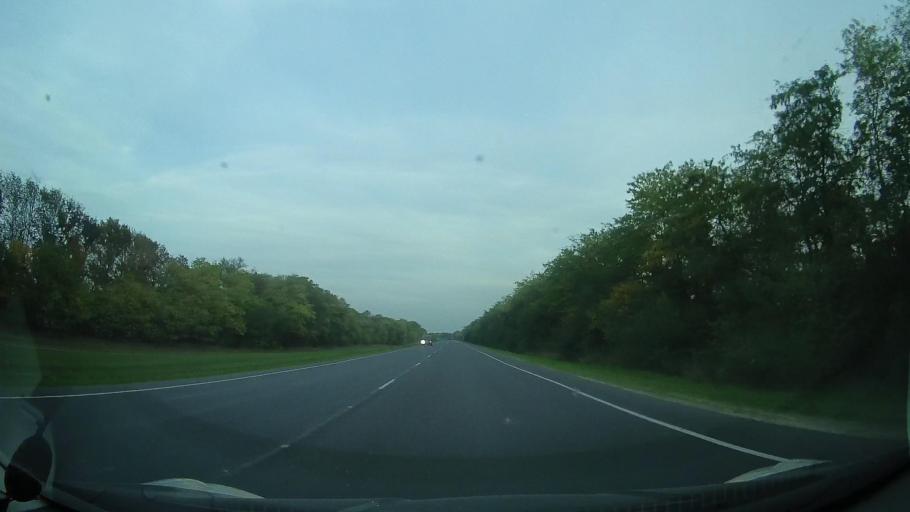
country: RU
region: Rostov
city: Kirovskaya
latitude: 46.9986
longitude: 39.9923
